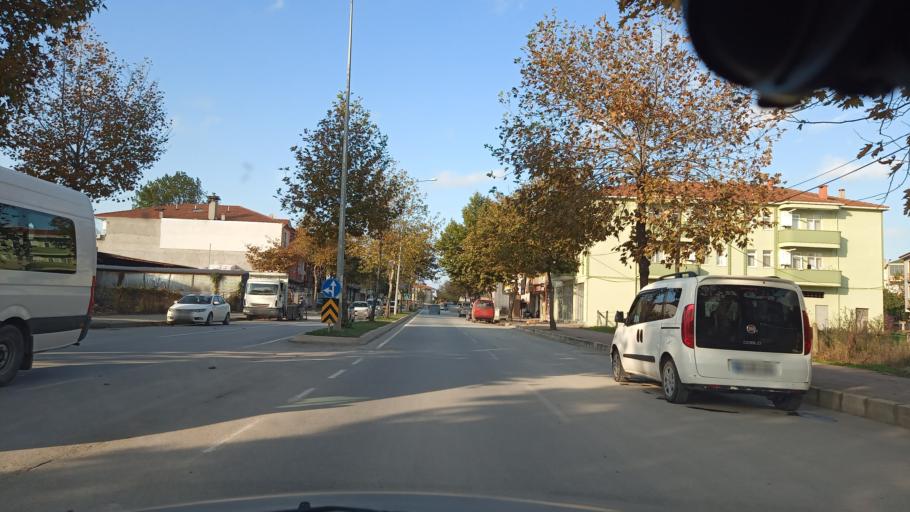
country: TR
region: Sakarya
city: Karasu
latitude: 41.1029
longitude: 30.6903
